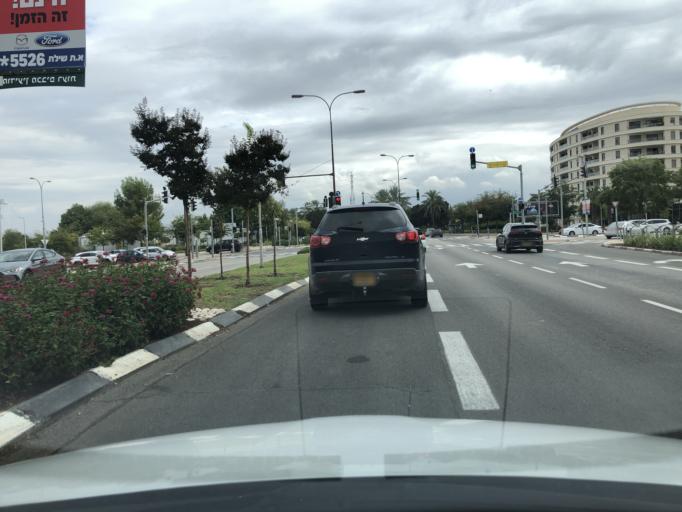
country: IL
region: Central District
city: Modiin
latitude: 31.9095
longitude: 35.0129
